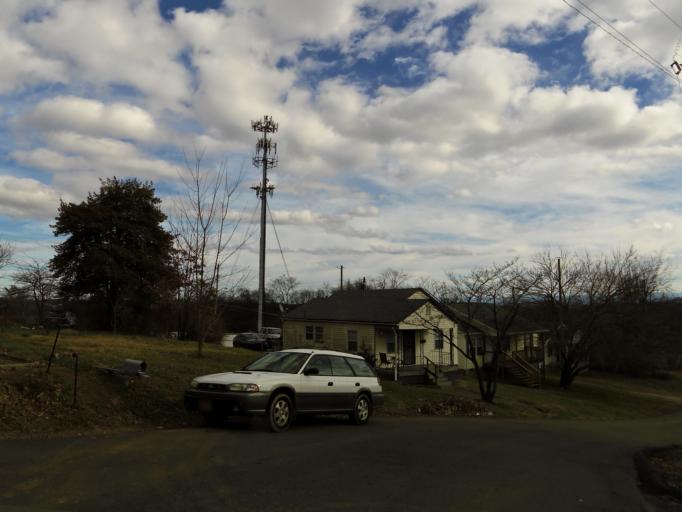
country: US
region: Tennessee
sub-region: Knox County
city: Knoxville
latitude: 35.9893
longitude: -83.9019
